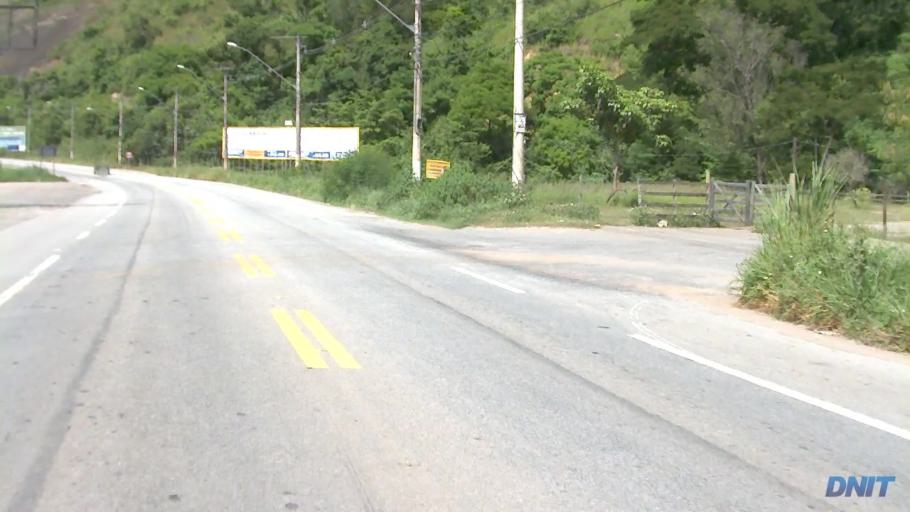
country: BR
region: Minas Gerais
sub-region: Timoteo
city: Timoteo
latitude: -19.5443
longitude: -42.6813
